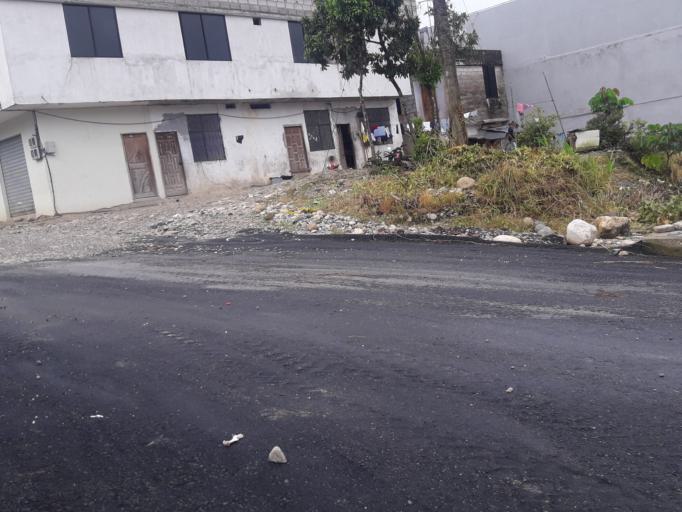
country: EC
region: Napo
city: Tena
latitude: -0.9993
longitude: -77.8084
